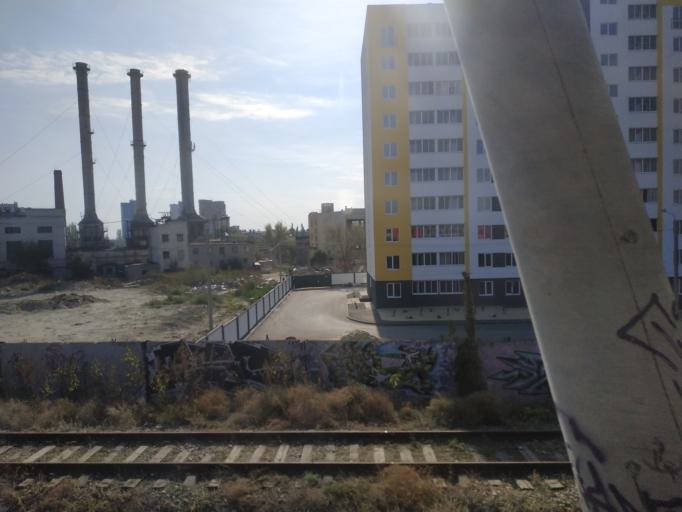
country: RU
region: Volgograd
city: Volgograd
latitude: 48.7323
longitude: 44.5341
